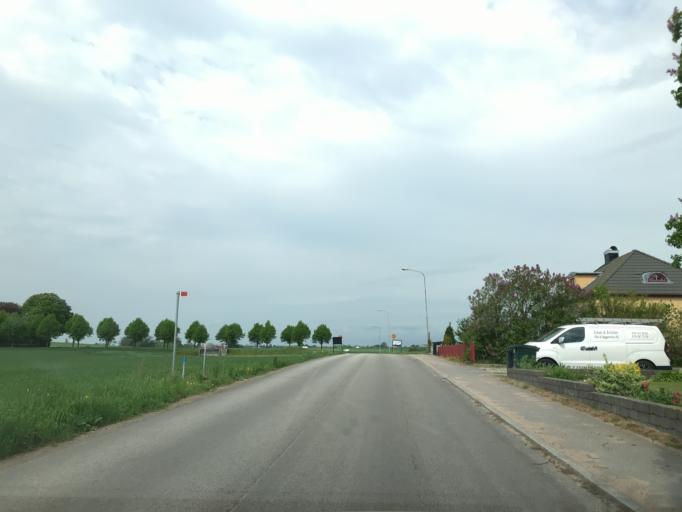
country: SE
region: Skane
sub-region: Svalovs Kommun
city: Svaloev
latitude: 55.8713
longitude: 13.1567
